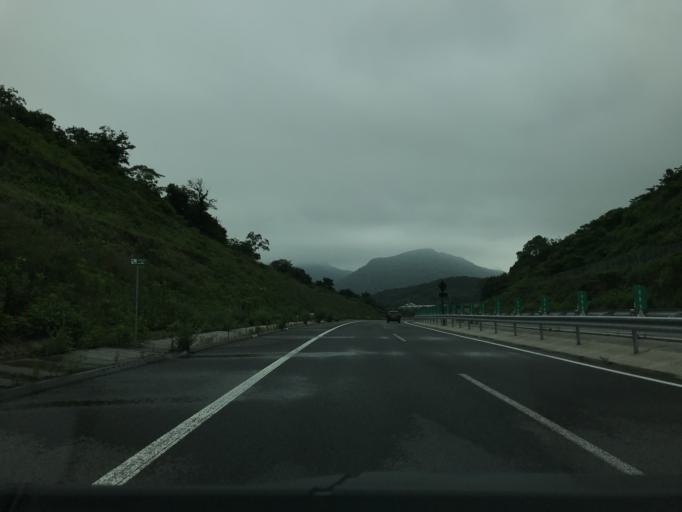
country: JP
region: Oita
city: Bungo-Takada-shi
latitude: 33.5037
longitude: 131.3096
